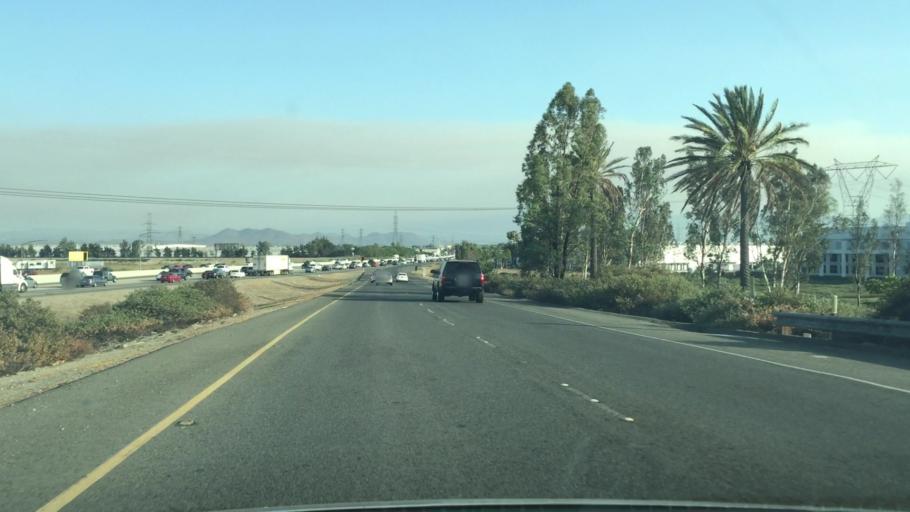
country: US
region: California
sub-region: Riverside County
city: Mira Loma
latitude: 34.0467
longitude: -117.5510
